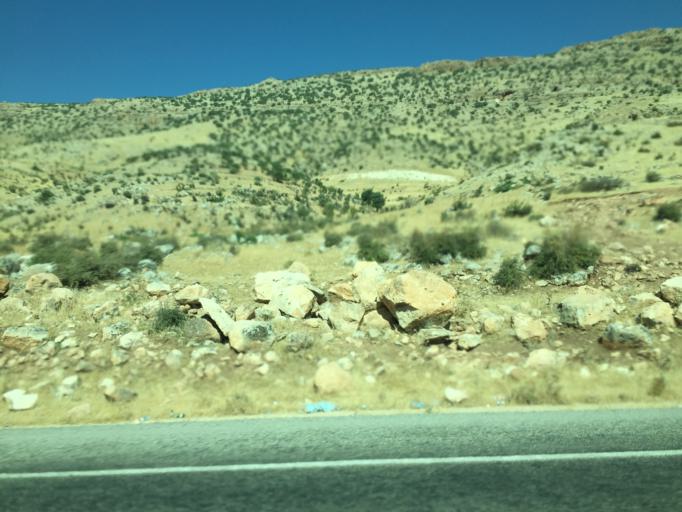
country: TR
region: Batman
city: Hasankeyf
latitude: 37.6890
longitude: 41.4553
